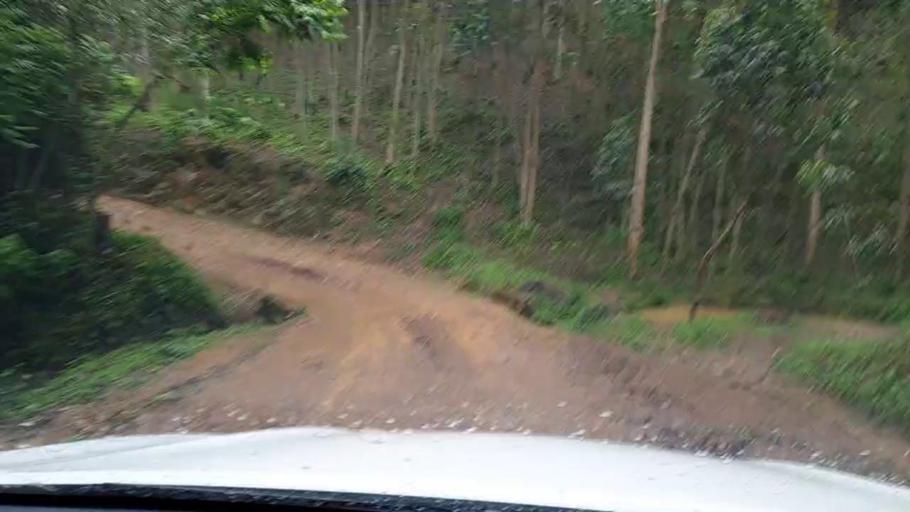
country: RW
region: Western Province
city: Cyangugu
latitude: -2.5556
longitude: 28.9782
